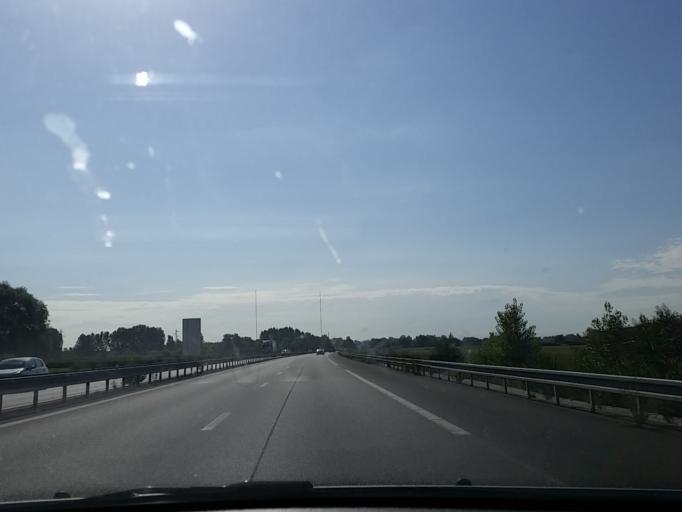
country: FR
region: Centre
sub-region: Departement du Cher
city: Vignoux-sur-Barangeon
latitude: 47.1935
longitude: 2.1566
